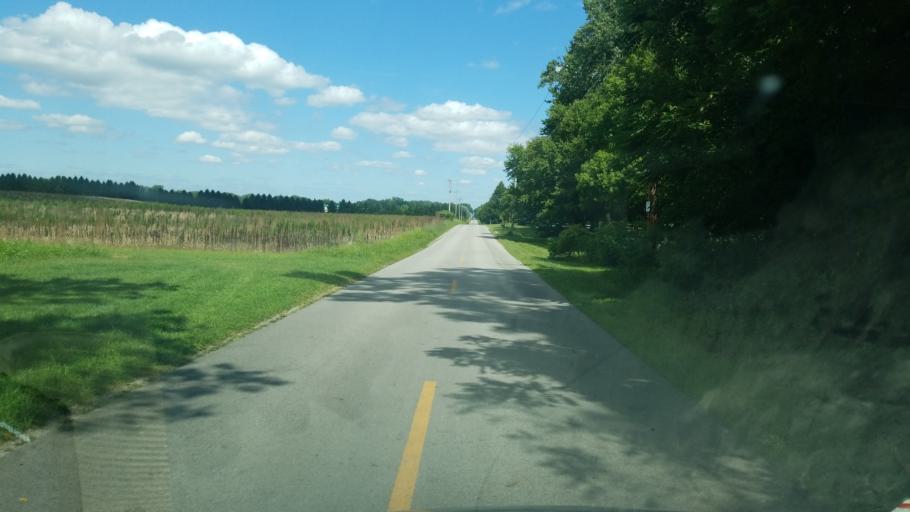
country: US
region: Ohio
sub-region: Henry County
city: Liberty Center
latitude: 41.4792
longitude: -83.9412
